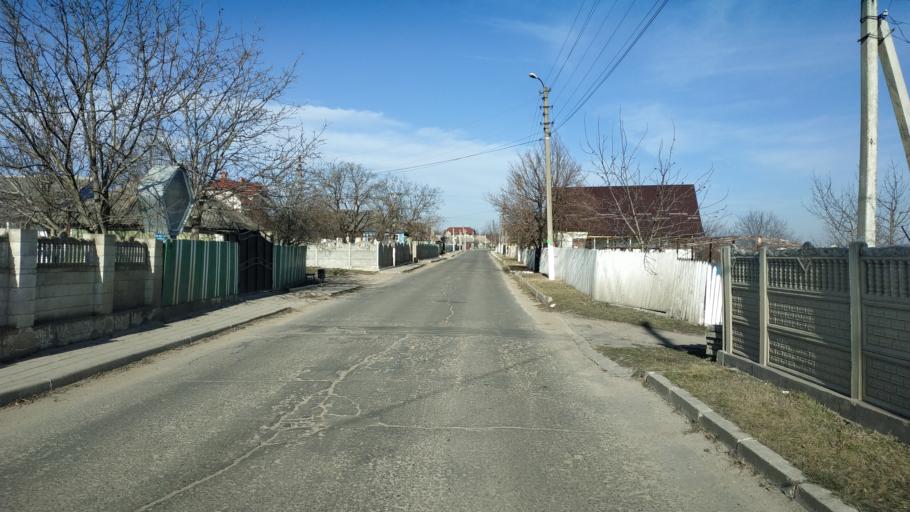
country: MD
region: Chisinau
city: Vatra
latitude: 47.0110
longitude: 28.6629
